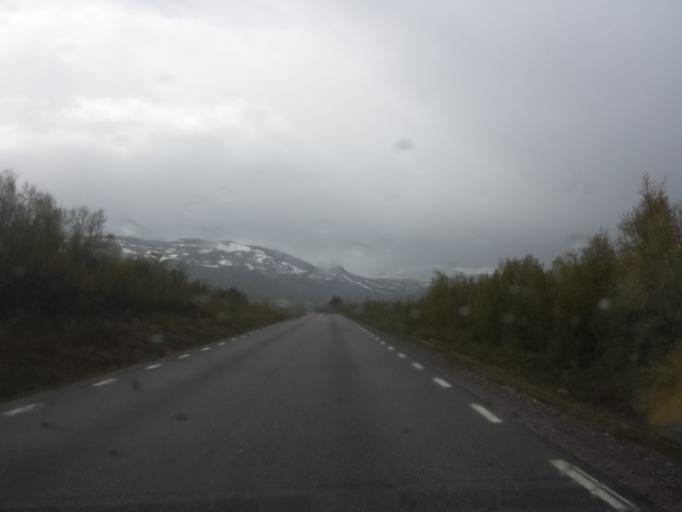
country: SE
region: Norrbotten
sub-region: Kiruna Kommun
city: Kiruna
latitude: 68.2330
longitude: 19.6049
